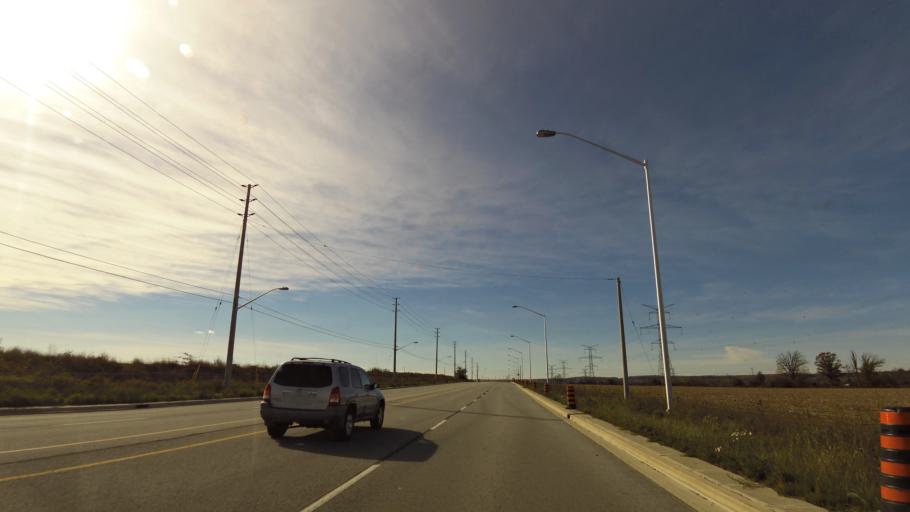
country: CA
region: Ontario
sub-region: Halton
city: Milton
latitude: 43.5434
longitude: -79.8945
